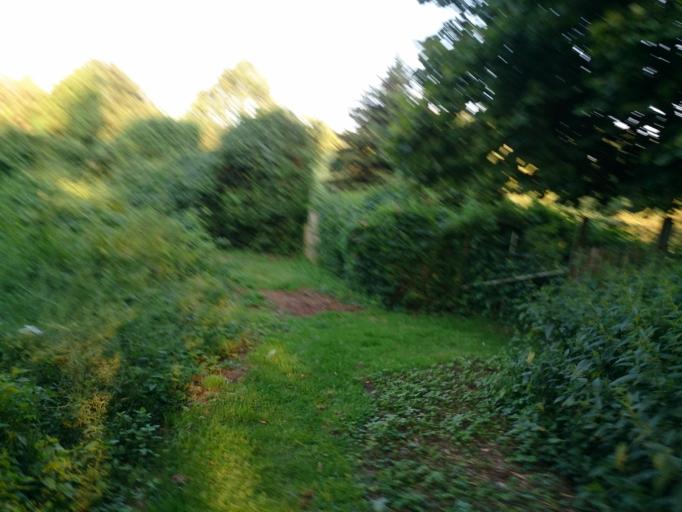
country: DE
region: Hamburg
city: Altona
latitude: 53.4798
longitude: 9.8974
